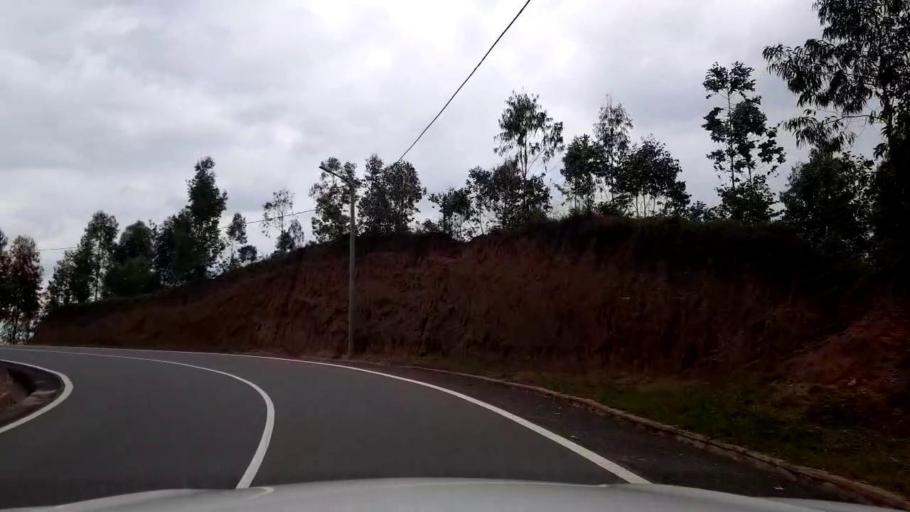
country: RW
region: Western Province
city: Kibuye
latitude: -1.9296
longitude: 29.3726
